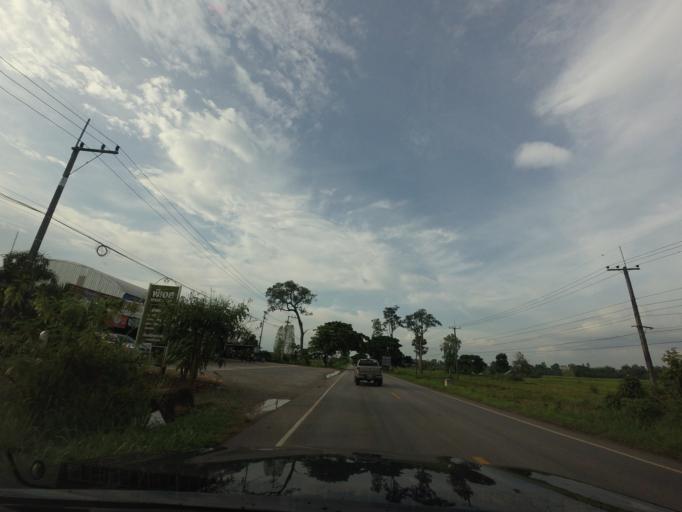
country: TH
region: Changwat Udon Thani
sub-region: Amphoe Ban Phue
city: Ban Phue
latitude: 17.7609
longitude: 102.3976
